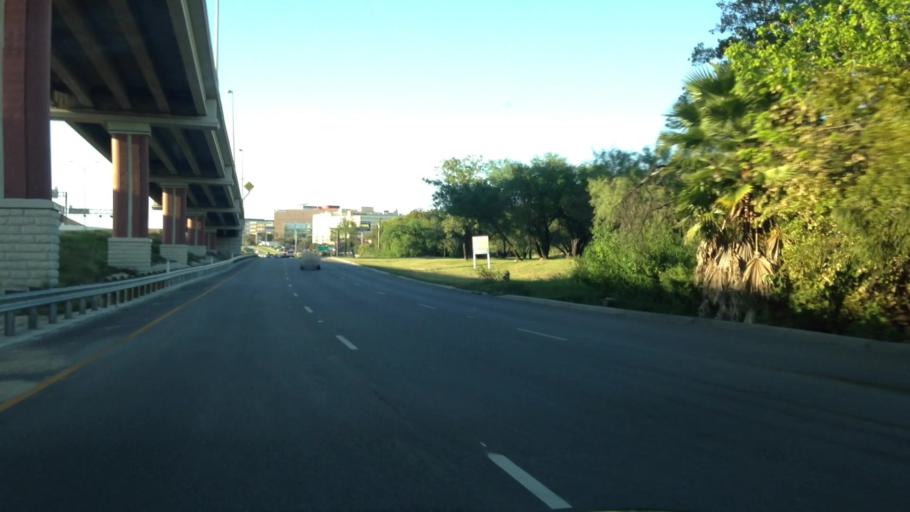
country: US
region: Texas
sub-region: Bexar County
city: Castle Hills
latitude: 29.5247
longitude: -98.4816
